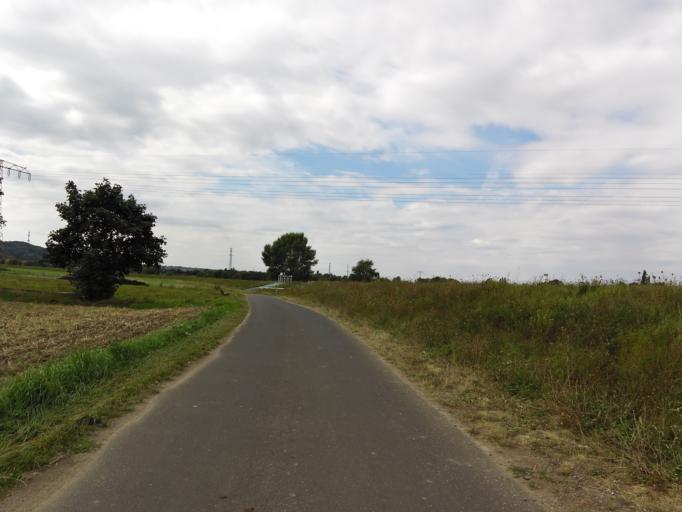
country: DE
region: Saxony
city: Radebeul
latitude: 51.0997
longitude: 13.6229
